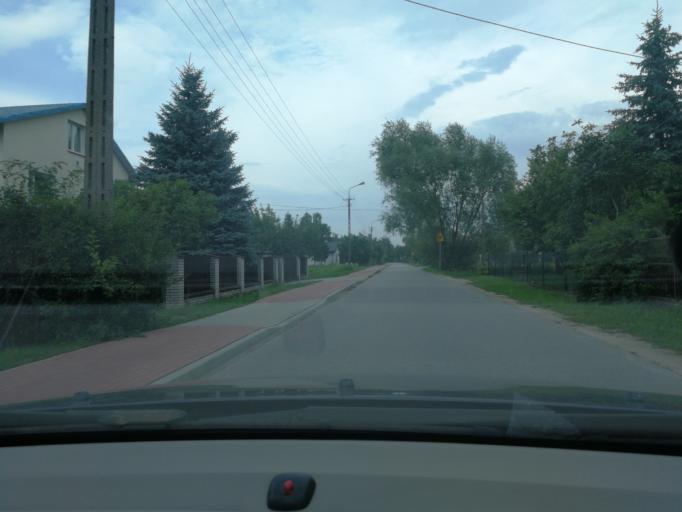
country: PL
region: Masovian Voivodeship
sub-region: Powiat grodziski
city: Grodzisk Mazowiecki
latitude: 52.1260
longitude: 20.6149
